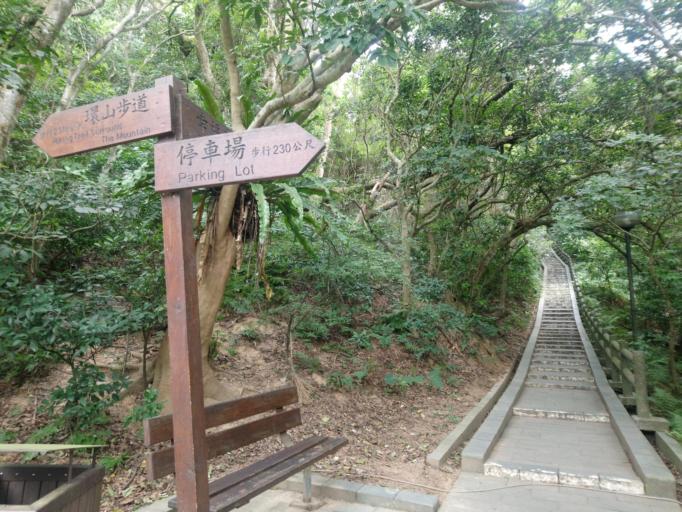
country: TW
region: Taiwan
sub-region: Hsinchu
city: Hsinchu
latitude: 24.7915
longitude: 120.9870
